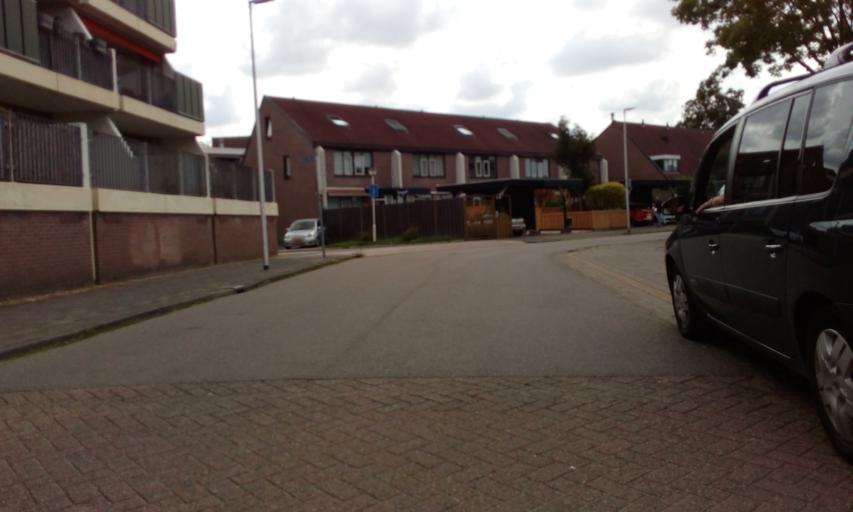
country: NL
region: South Holland
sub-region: Gemeente Zoetermeer
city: Zoetermeer
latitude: 52.0657
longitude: 4.4784
